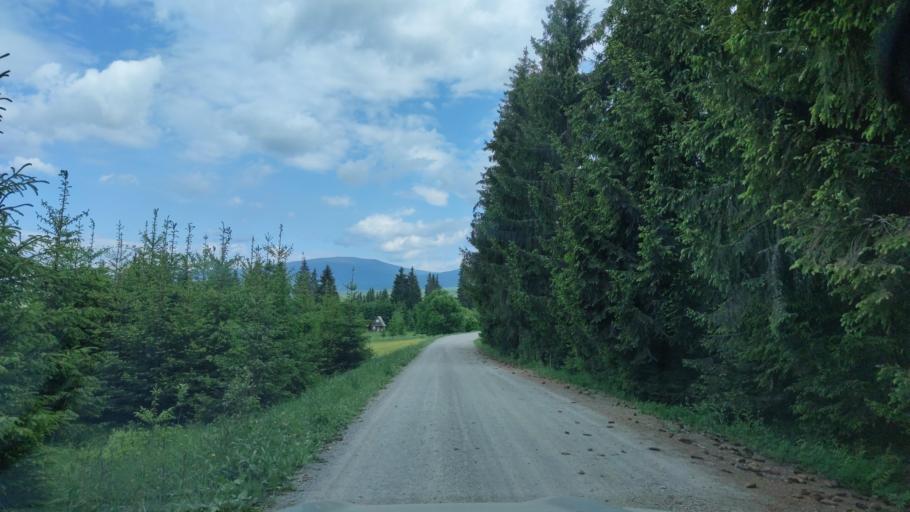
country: RO
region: Harghita
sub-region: Comuna Joseni
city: Joseni
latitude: 46.6664
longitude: 25.3821
